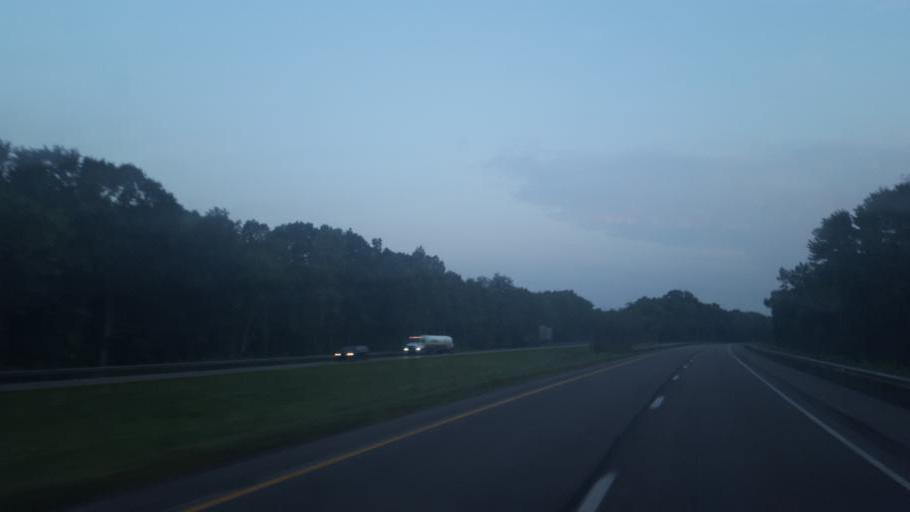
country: US
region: Pennsylvania
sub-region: Mercer County
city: Stoneboro
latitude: 41.4154
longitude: -80.1610
